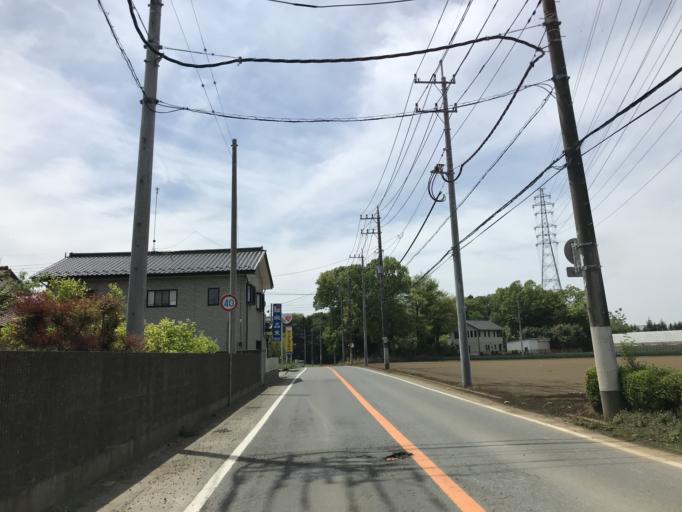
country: JP
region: Ibaraki
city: Mitsukaido
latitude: 35.9875
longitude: 139.9546
